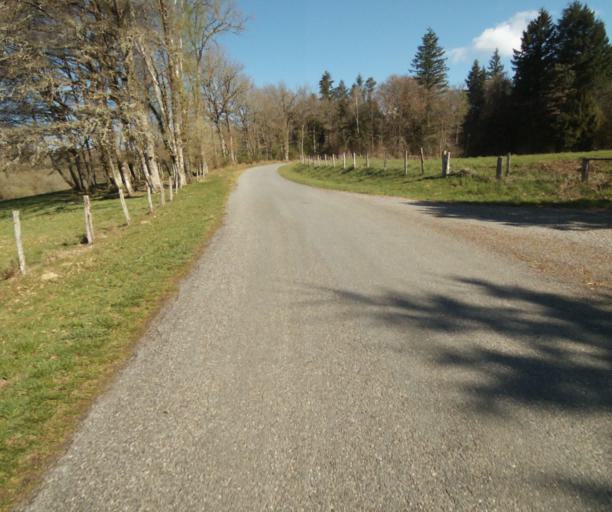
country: FR
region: Limousin
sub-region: Departement de la Correze
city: Correze
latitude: 45.2441
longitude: 1.9201
